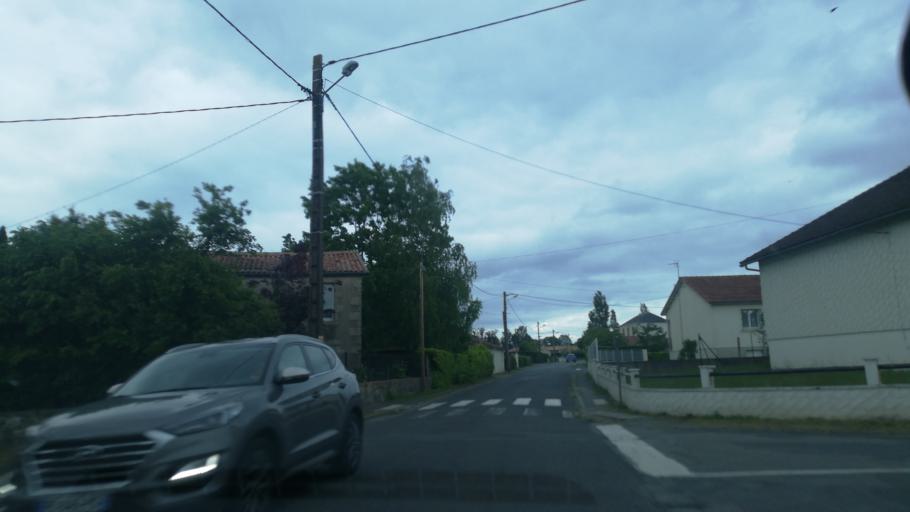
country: FR
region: Poitou-Charentes
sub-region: Departement des Deux-Sevres
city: Courlay
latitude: 46.7666
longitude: -0.5227
